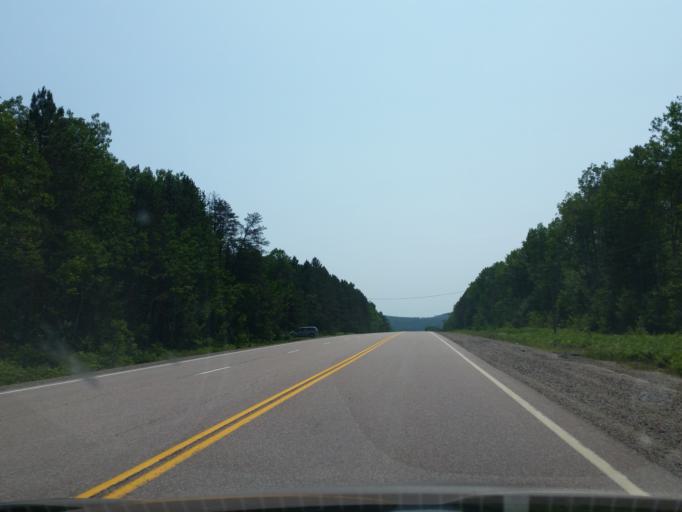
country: CA
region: Ontario
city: Deep River
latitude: 46.1739
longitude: -77.8294
